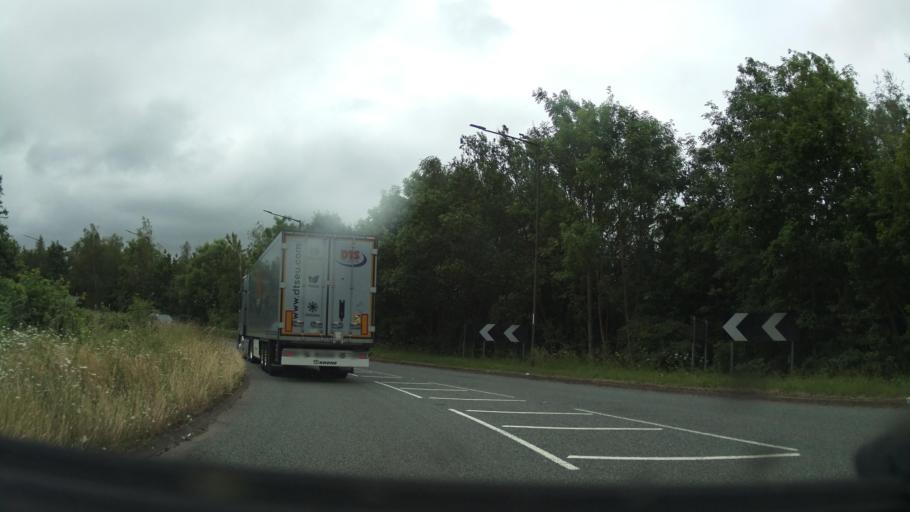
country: GB
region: England
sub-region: Derbyshire
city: Rodsley
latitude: 52.8806
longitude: -1.7033
